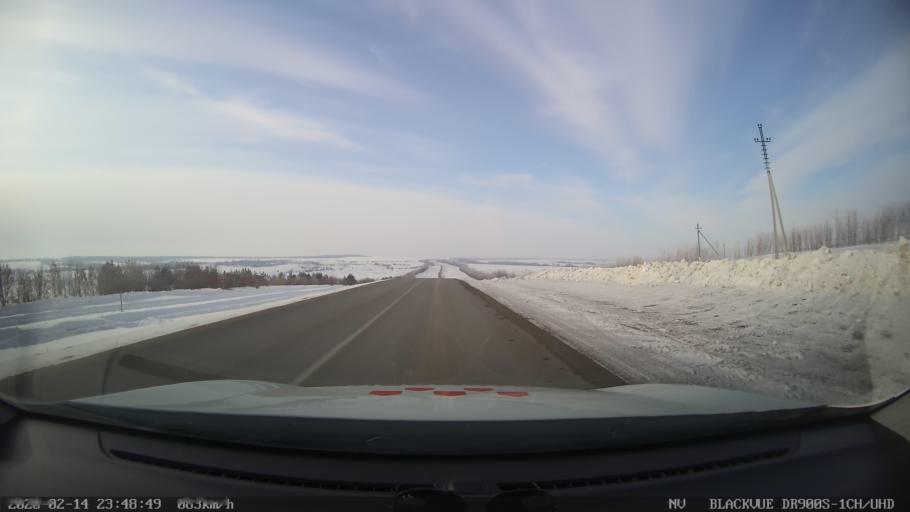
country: RU
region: Tatarstan
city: Kuybyshevskiy Zaton
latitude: 55.2497
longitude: 49.1957
